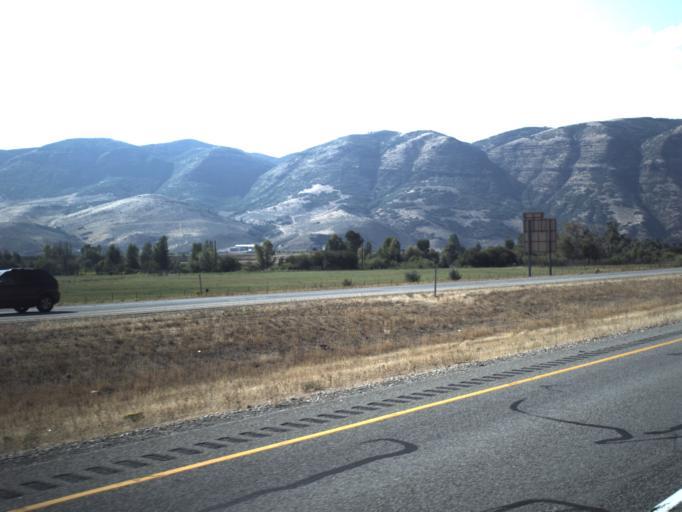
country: US
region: Utah
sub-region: Summit County
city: Coalville
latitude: 41.0295
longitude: -111.5013
